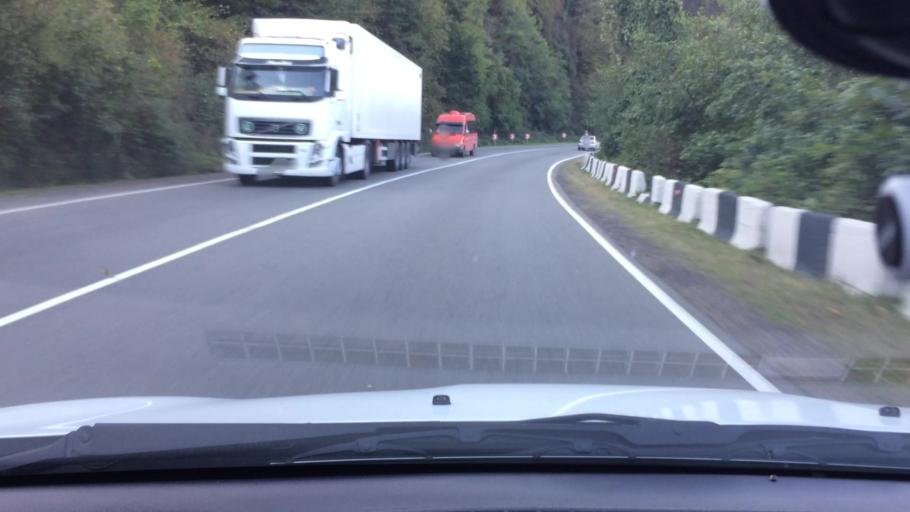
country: GE
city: Shorapani
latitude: 42.0939
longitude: 43.1032
